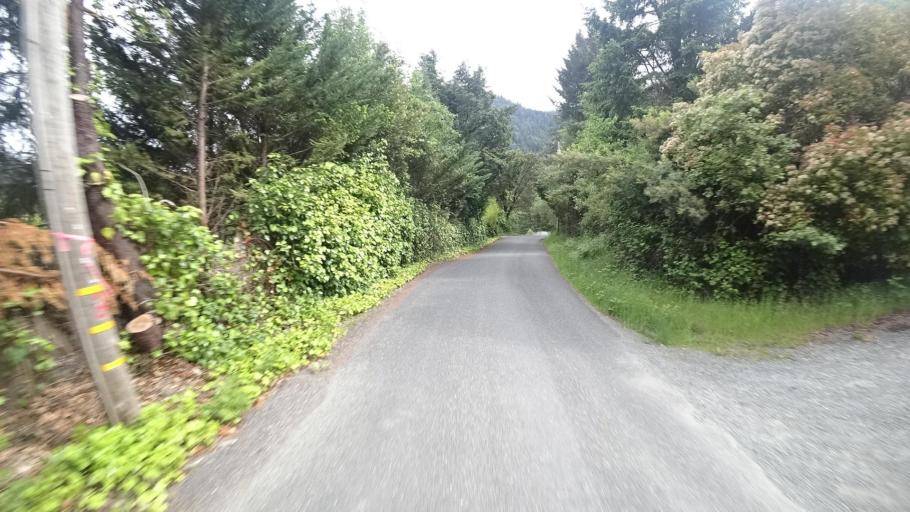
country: US
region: California
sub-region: Humboldt County
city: Willow Creek
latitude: 40.9416
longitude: -123.6130
